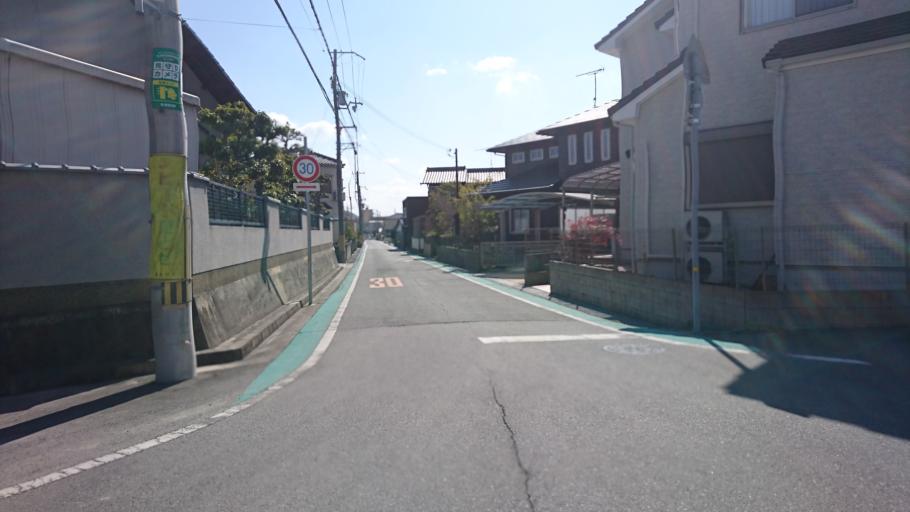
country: JP
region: Hyogo
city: Kakogawacho-honmachi
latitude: 34.8216
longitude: 134.8201
